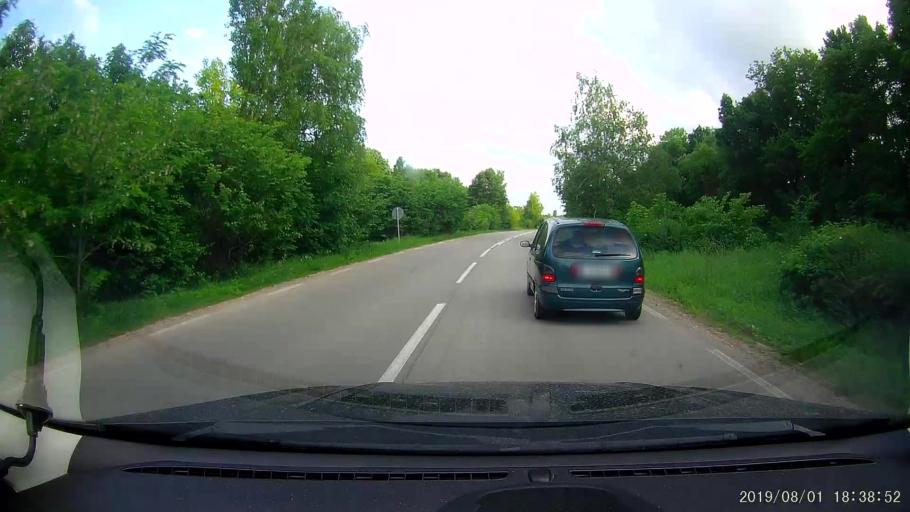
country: BG
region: Shumen
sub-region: Obshtina Khitrino
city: Gara Khitrino
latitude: 43.3965
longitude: 26.9170
